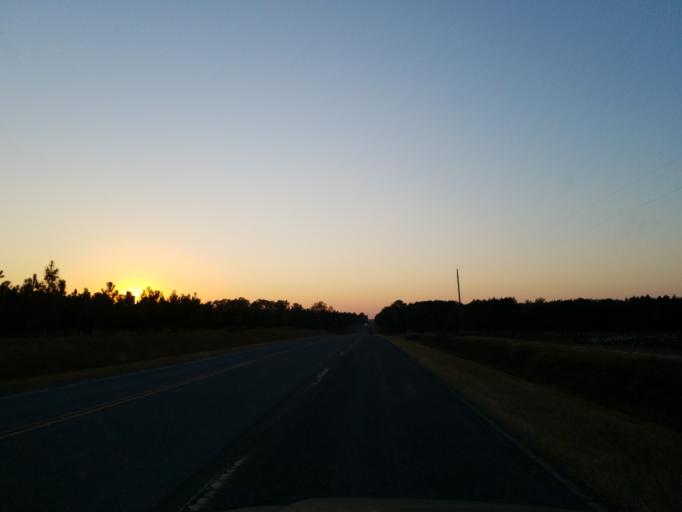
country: US
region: Georgia
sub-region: Ben Hill County
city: Fitzgerald
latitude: 31.7204
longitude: -83.4152
